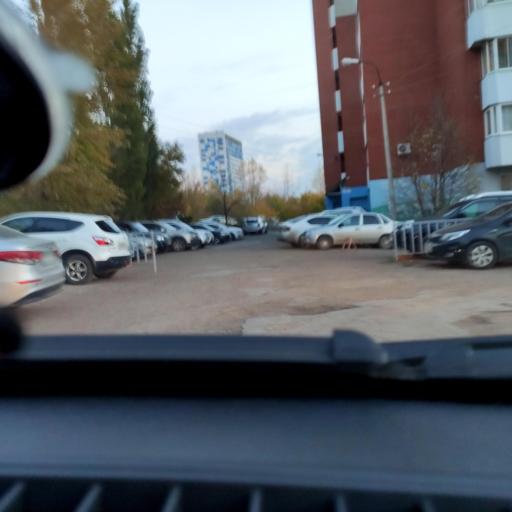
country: RU
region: Bashkortostan
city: Ufa
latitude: 54.7775
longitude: 56.0466
